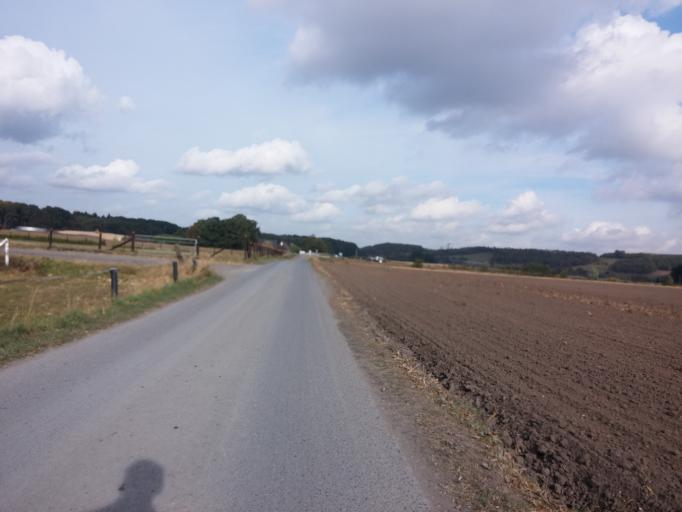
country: DE
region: North Rhine-Westphalia
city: Dorsten
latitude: 51.6429
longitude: 7.0114
